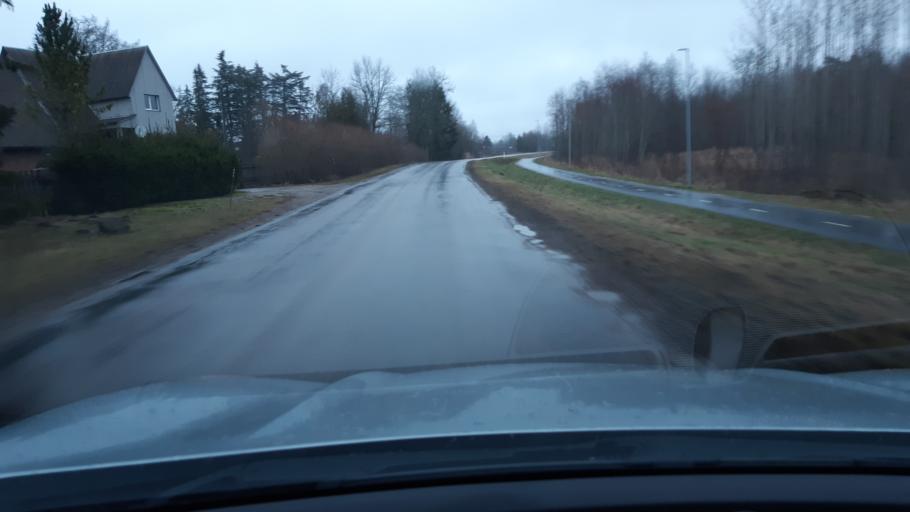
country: EE
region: Raplamaa
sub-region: Kohila vald
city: Kohila
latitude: 59.1597
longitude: 24.6606
